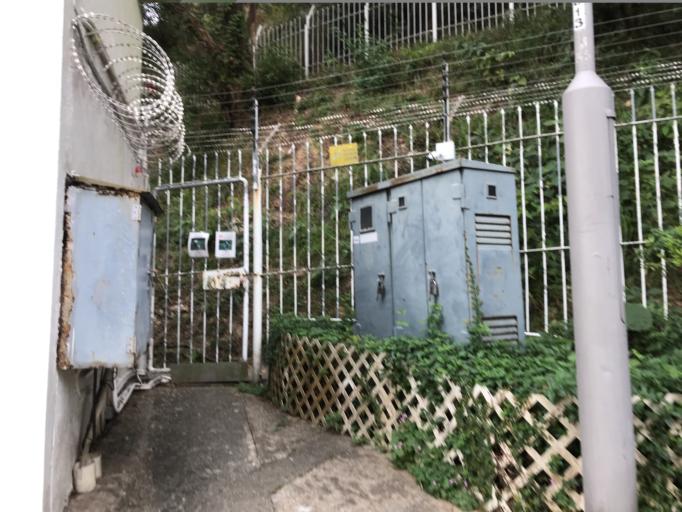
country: HK
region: Tai Po
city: Tai Po
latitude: 22.4649
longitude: 114.1590
